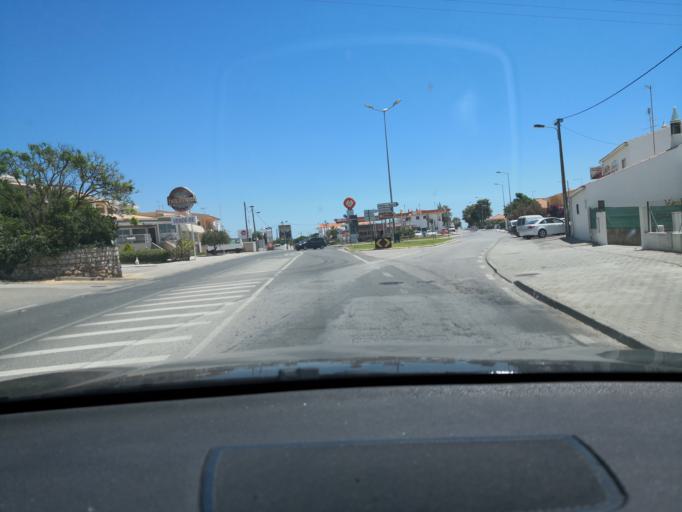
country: PT
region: Faro
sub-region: Albufeira
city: Ferreiras
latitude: 37.1040
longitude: -8.1951
